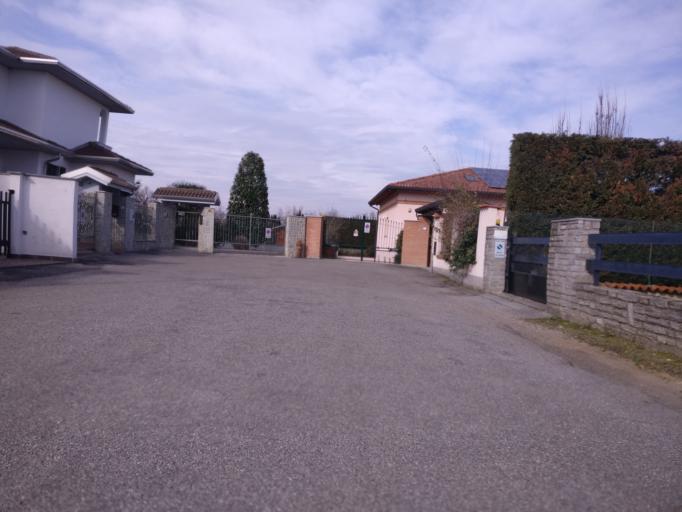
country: IT
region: Lombardy
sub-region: Citta metropolitana di Milano
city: Arluno
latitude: 45.5109
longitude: 8.9369
